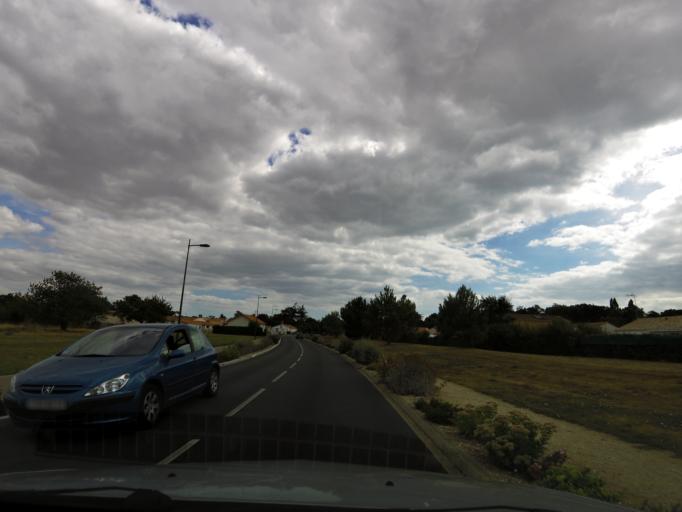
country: FR
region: Pays de la Loire
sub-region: Departement de la Vendee
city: Longeville-sur-Mer
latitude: 46.4128
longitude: -1.4949
